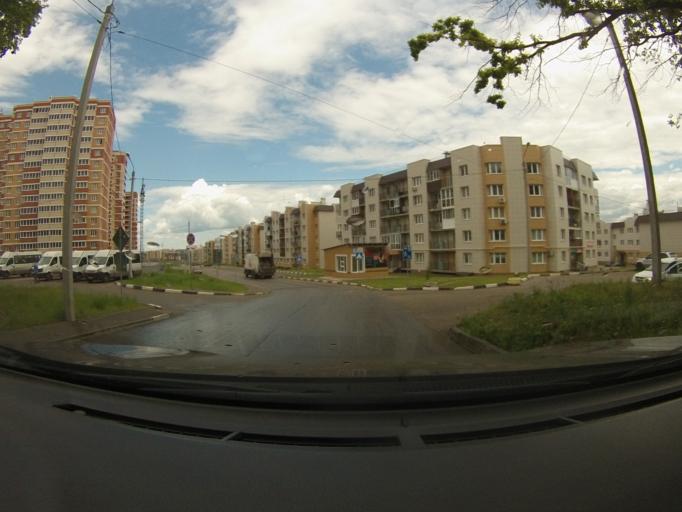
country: RU
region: Tula
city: Tula
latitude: 54.1721
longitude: 37.6541
